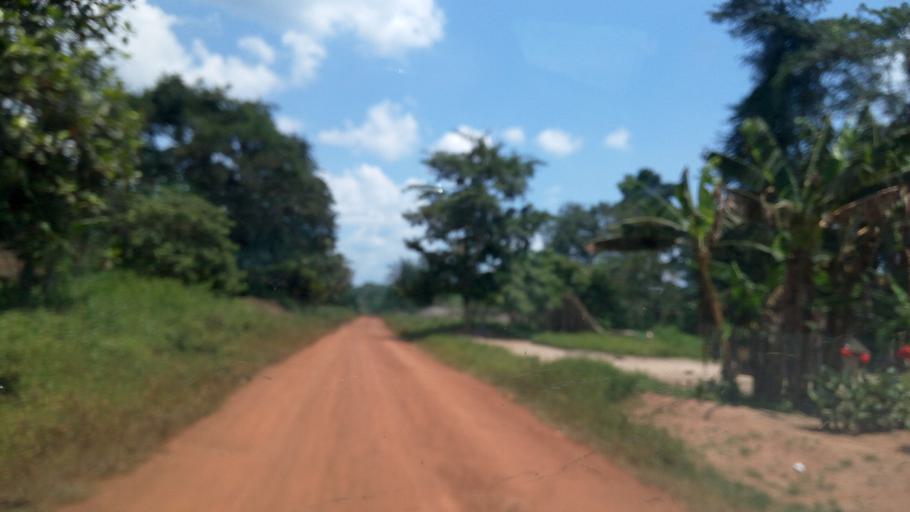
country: CD
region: Equateur
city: Gemena
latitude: 3.3172
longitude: 19.4199
